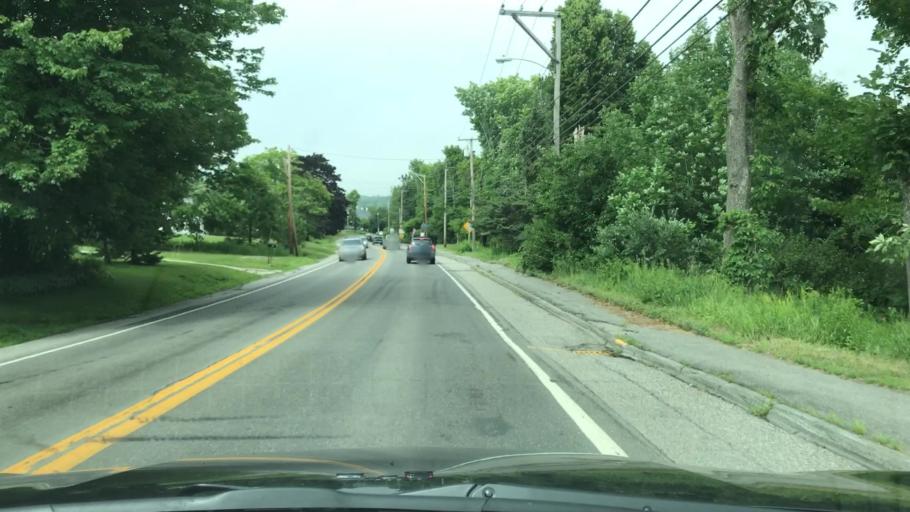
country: US
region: Maine
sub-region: Waldo County
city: Belfast
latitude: 44.4524
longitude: -68.9322
